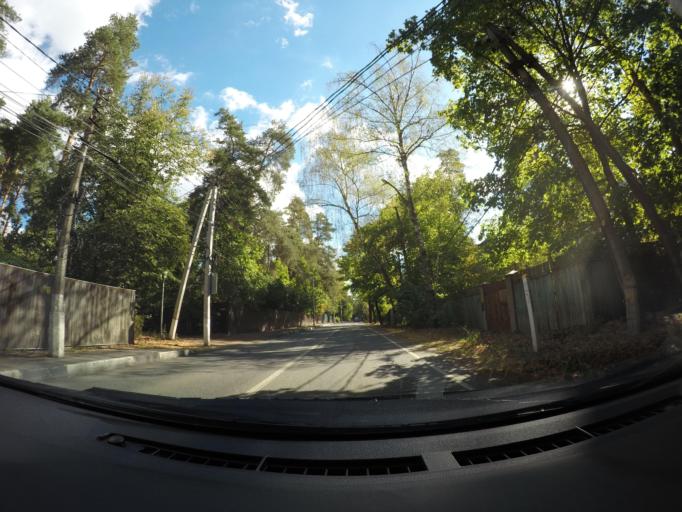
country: RU
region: Moskovskaya
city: Zhukovskiy
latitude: 55.6061
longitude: 38.1374
